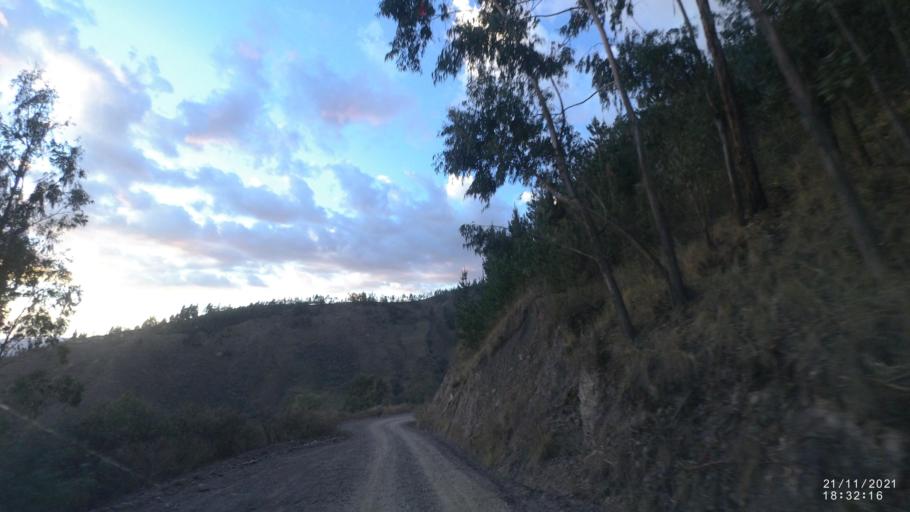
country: BO
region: Cochabamba
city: Cochabamba
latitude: -17.3096
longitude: -66.2184
